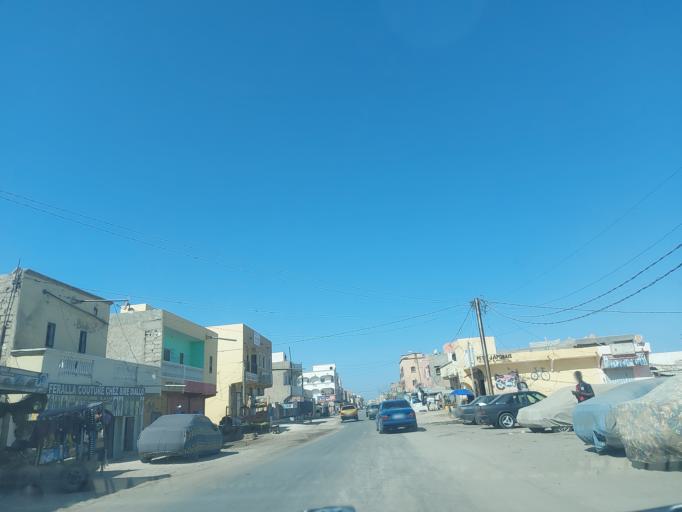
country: MR
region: Nouakchott
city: Nouakchott
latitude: 18.0762
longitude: -15.9963
